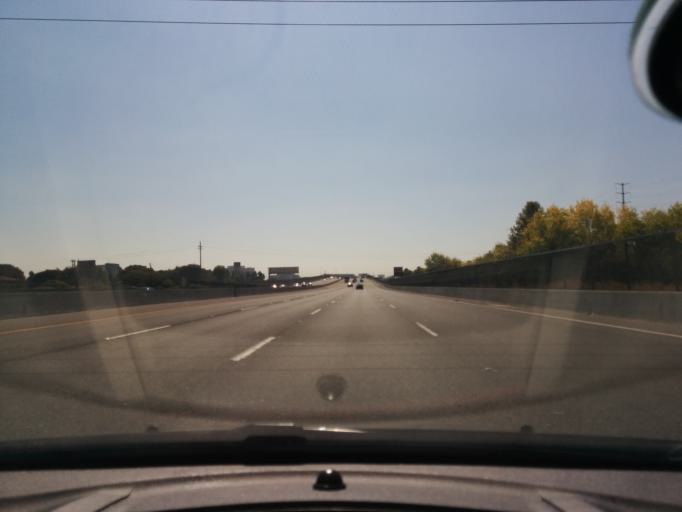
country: US
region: California
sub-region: Santa Clara County
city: San Jose
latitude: 37.3594
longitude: -121.9154
